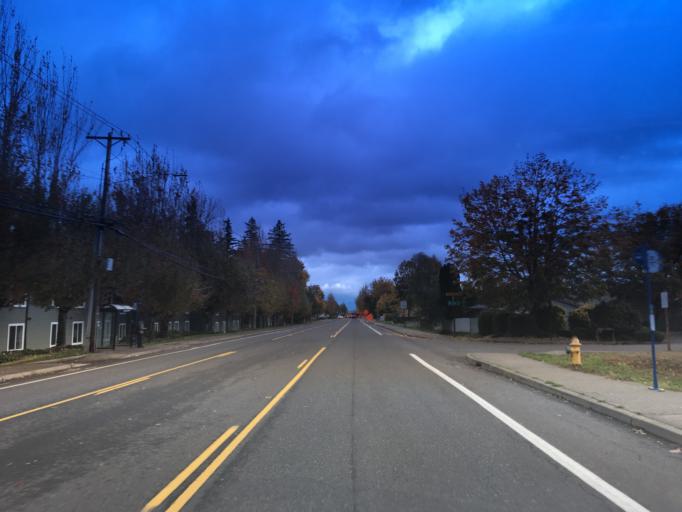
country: US
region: Oregon
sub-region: Multnomah County
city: Fairview
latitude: 45.5360
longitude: -122.4267
